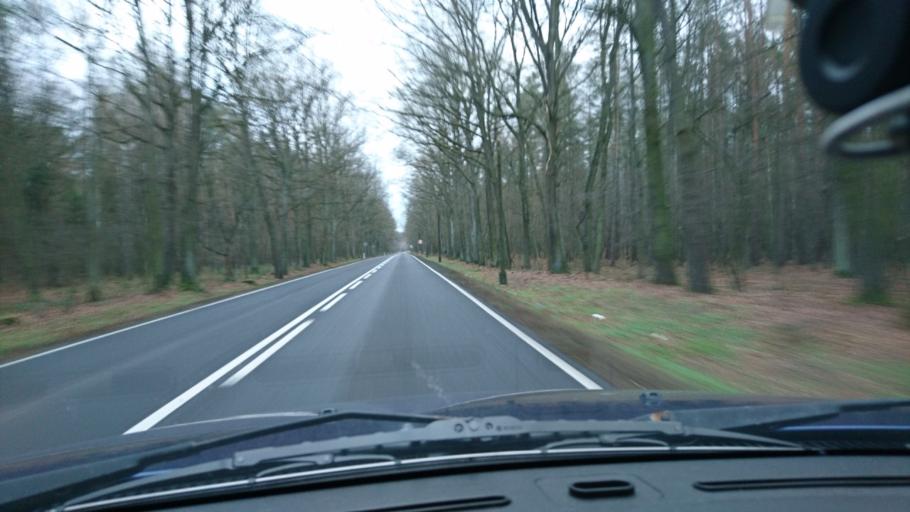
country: PL
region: Opole Voivodeship
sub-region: Powiat kluczborski
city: Kluczbork
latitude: 50.9487
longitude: 18.3145
